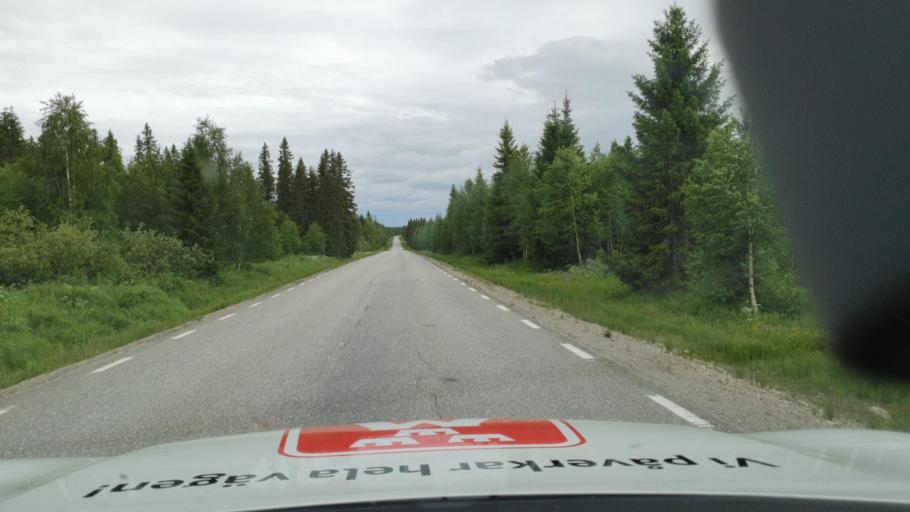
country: SE
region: Vaesterbotten
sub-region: Lycksele Kommun
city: Soderfors
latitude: 64.3542
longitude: 18.1254
